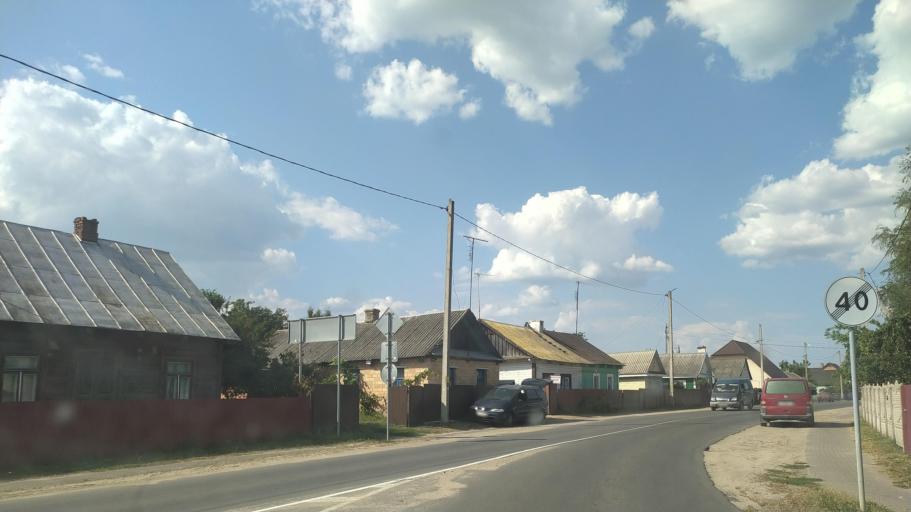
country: BY
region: Brest
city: Drahichyn
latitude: 52.1897
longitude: 25.1468
